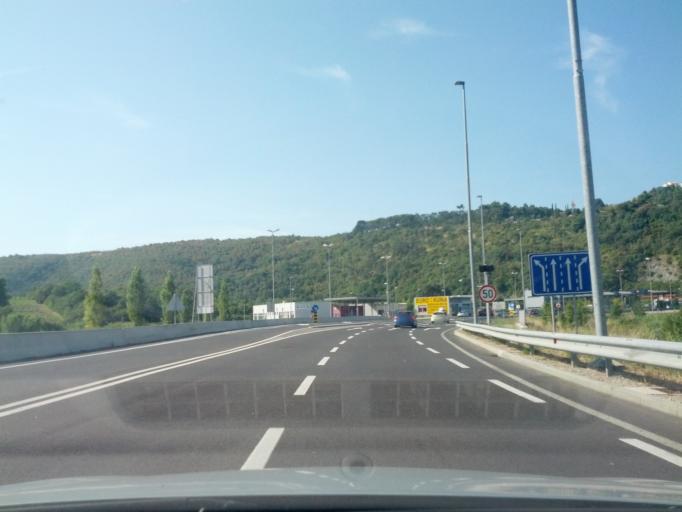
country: HR
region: Istarska
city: Buje
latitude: 45.4571
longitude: 13.6581
